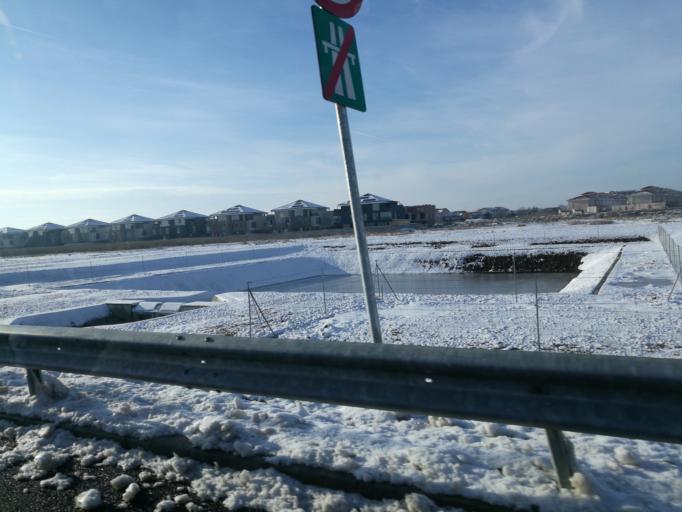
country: RO
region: Ilfov
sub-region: Voluntari City
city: Voluntari
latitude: 44.4952
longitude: 26.1506
